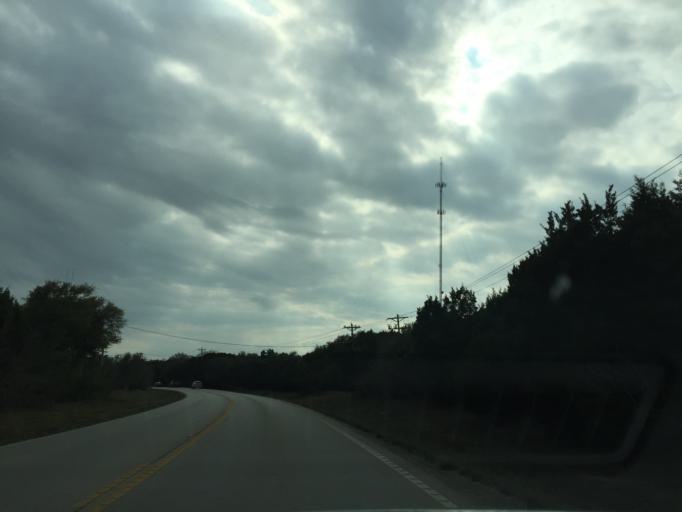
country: US
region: Texas
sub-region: Hays County
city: Dripping Springs
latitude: 30.1366
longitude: -98.0066
